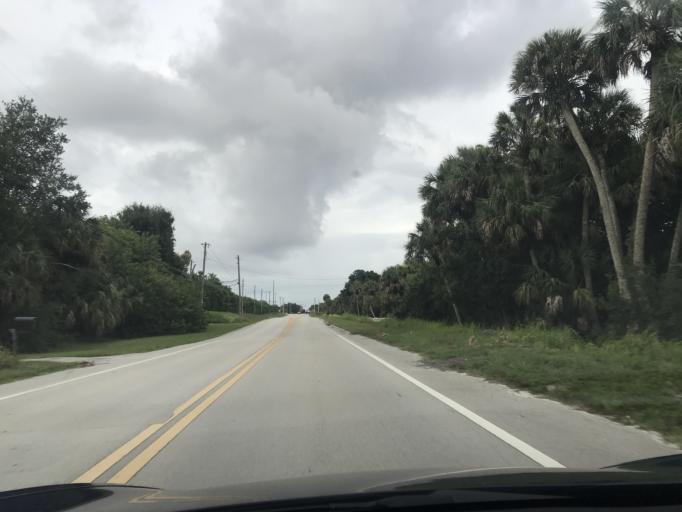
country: US
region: Florida
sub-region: Indian River County
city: Vero Beach South
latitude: 27.6167
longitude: -80.4511
